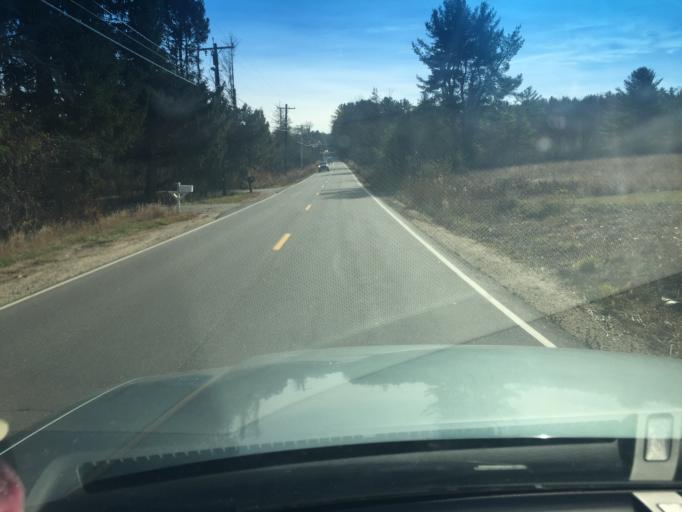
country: US
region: Maine
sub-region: York County
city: Eliot
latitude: 43.1838
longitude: -70.7406
